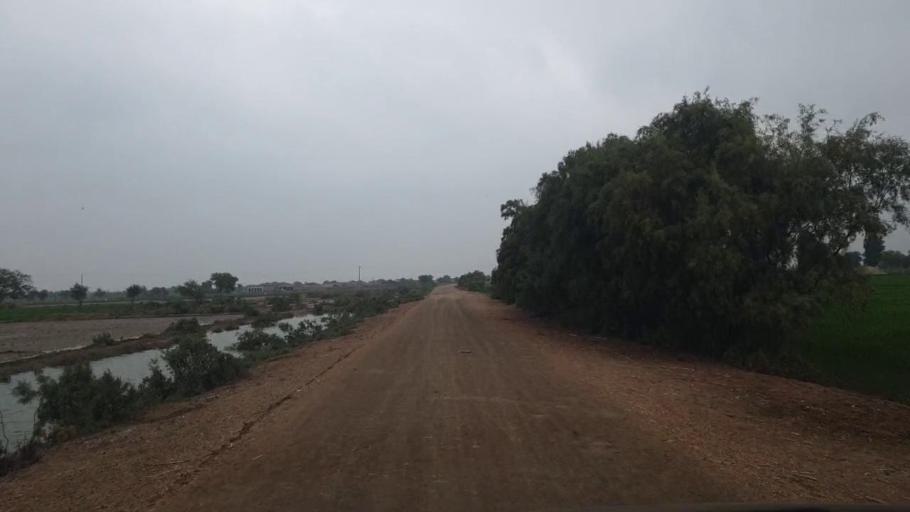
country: PK
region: Sindh
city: Shahdadpur
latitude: 25.9024
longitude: 68.6911
